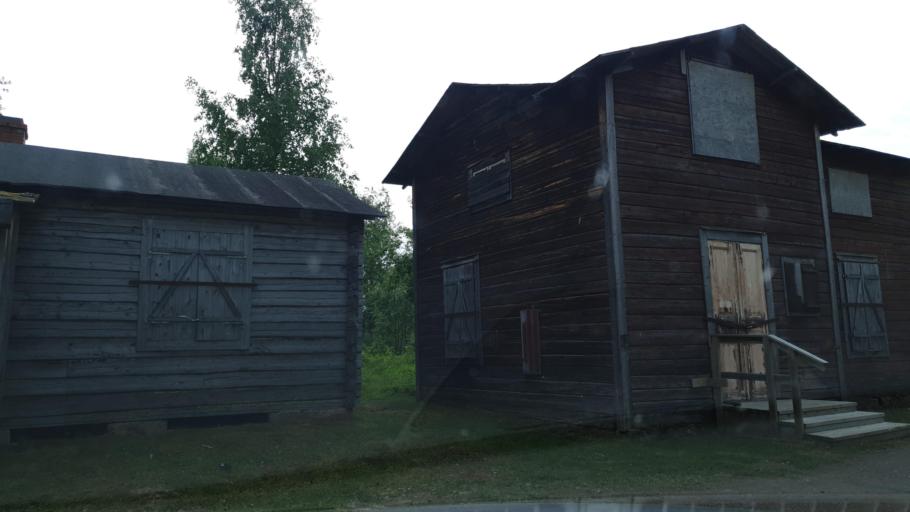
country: SE
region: Norrbotten
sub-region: Gallivare Kommun
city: Malmberget
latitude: 67.1763
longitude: 20.6657
